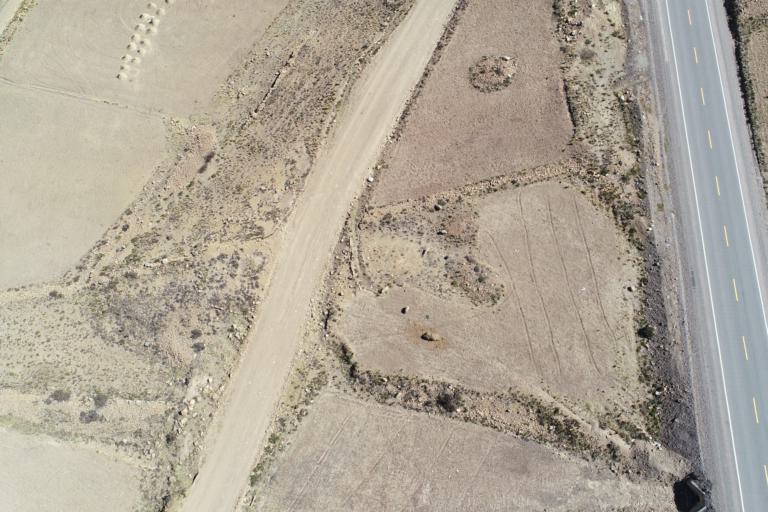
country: BO
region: La Paz
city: Achacachi
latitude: -15.8834
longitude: -68.8144
